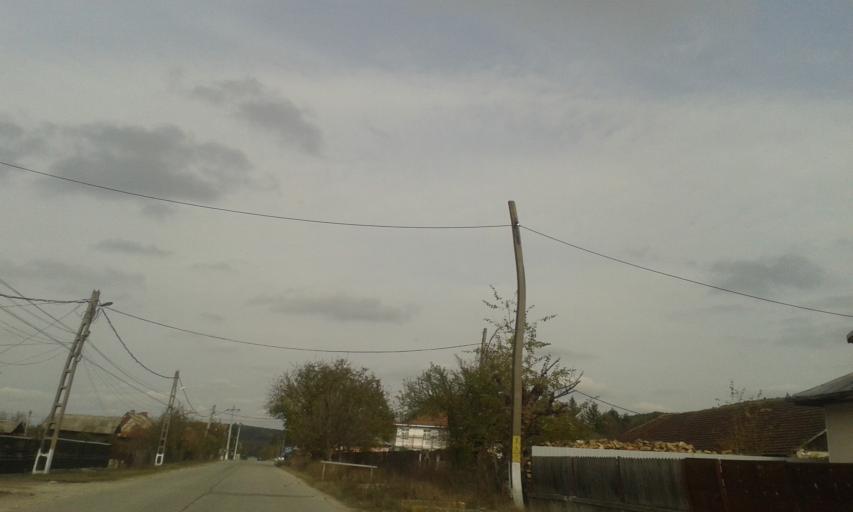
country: RO
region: Gorj
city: Logresti
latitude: 44.8727
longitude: 23.7063
